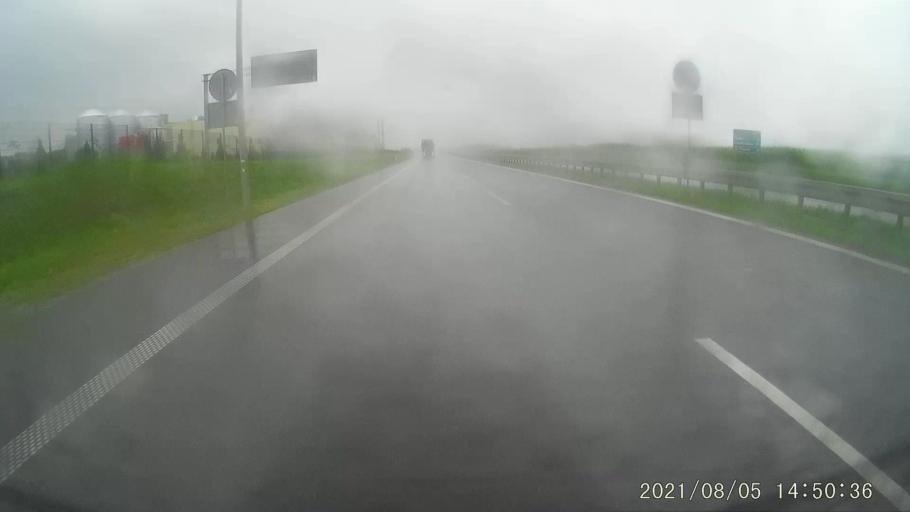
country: PL
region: Opole Voivodeship
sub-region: Powiat nyski
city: Nysa
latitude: 50.4771
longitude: 17.2624
